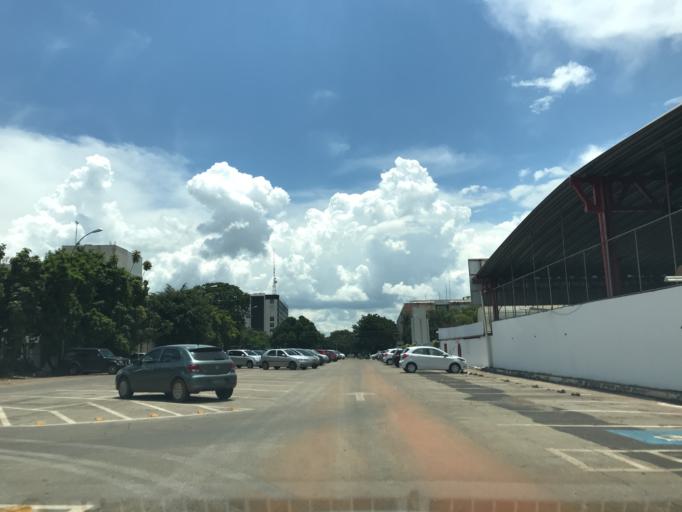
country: BR
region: Federal District
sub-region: Brasilia
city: Brasilia
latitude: -15.7968
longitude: -47.8977
